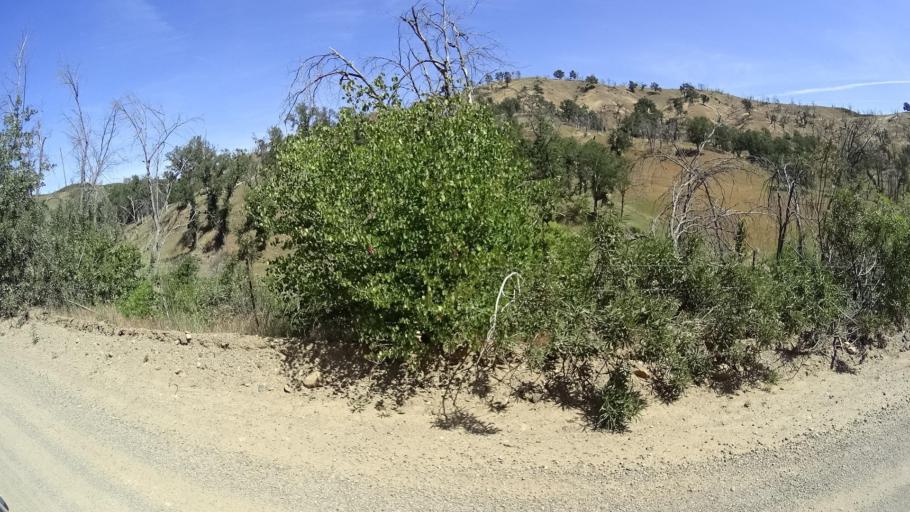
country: US
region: California
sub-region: Lake County
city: Middletown
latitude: 38.8109
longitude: -122.6172
